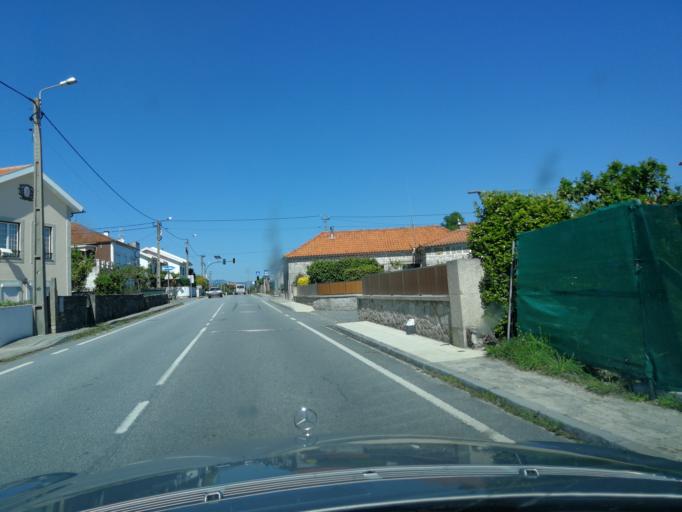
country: PT
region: Viana do Castelo
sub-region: Viana do Castelo
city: Darque
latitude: 41.7123
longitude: -8.7412
